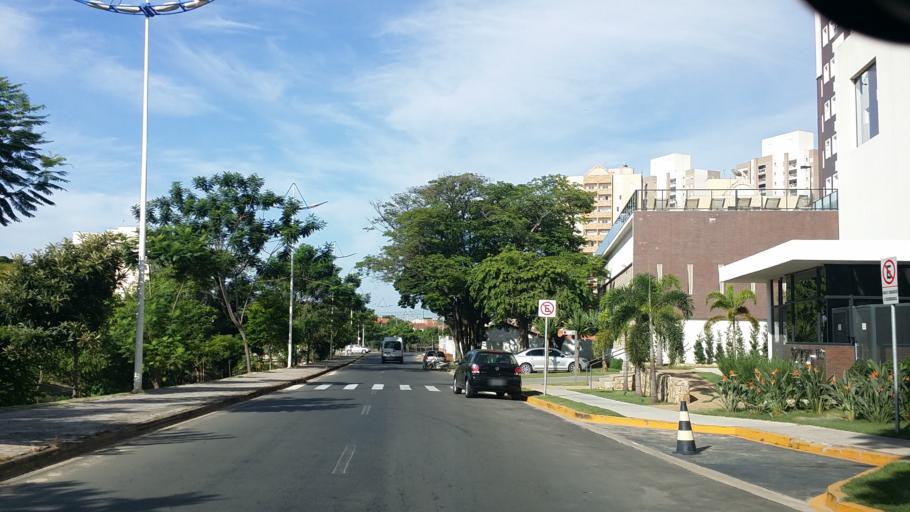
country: BR
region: Sao Paulo
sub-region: Indaiatuba
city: Indaiatuba
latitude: -23.0945
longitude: -47.2183
